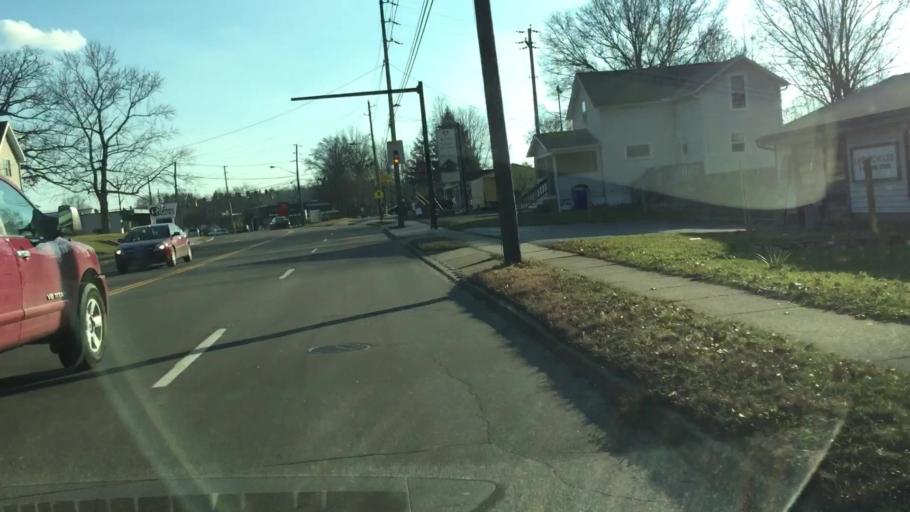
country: US
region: Ohio
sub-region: Portage County
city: Kent
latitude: 41.1444
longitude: -81.3584
